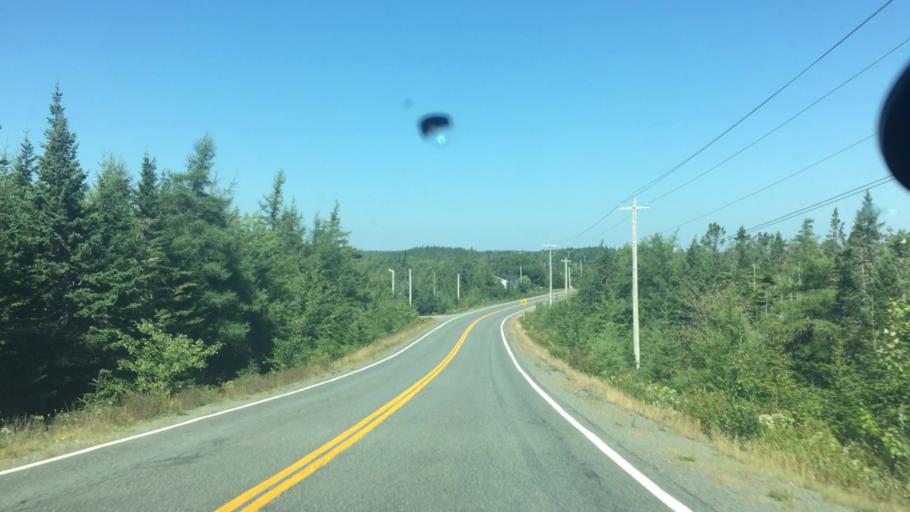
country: CA
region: Nova Scotia
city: Antigonish
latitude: 44.9961
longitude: -62.0990
